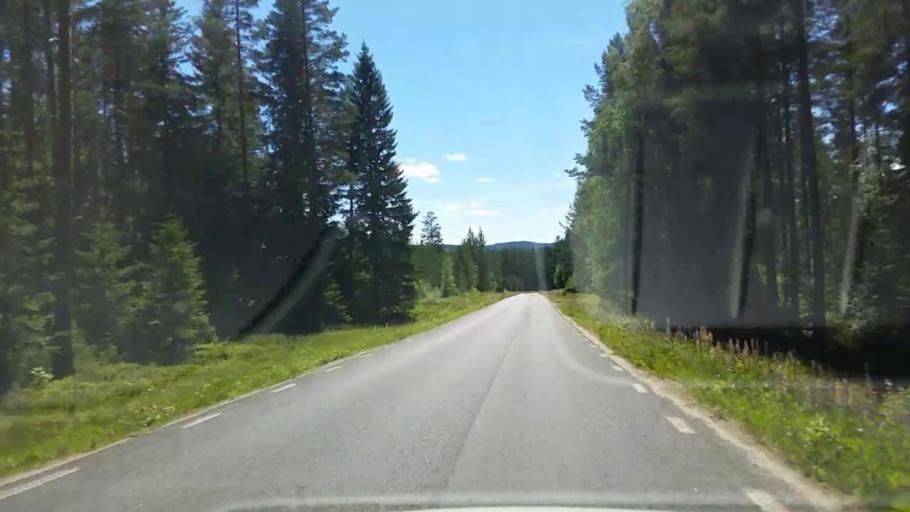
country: SE
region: Gaevleborg
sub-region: Ljusdals Kommun
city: Farila
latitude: 61.6714
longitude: 15.6155
